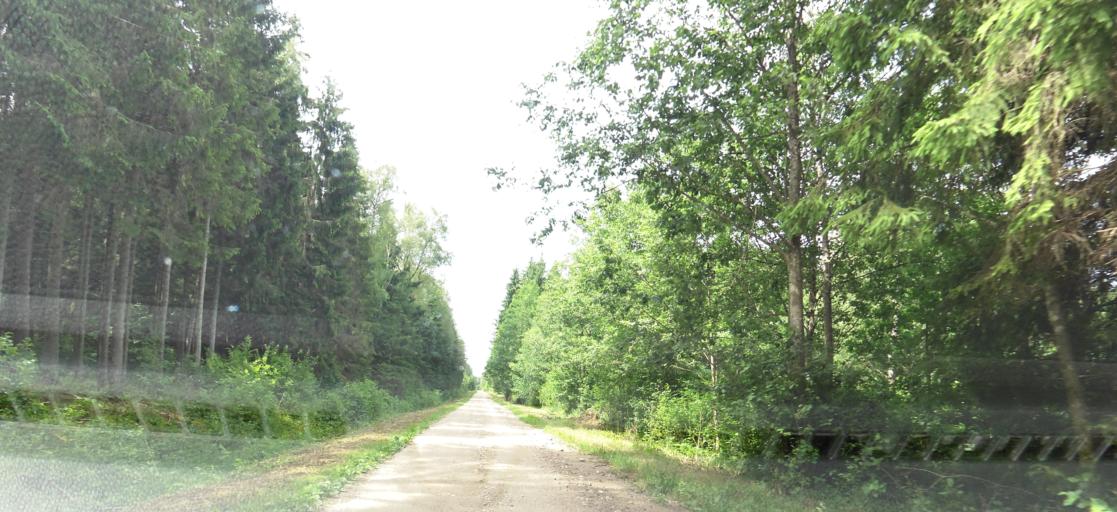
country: LT
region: Panevezys
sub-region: Birzai
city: Birzai
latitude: 56.2704
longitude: 24.7556
